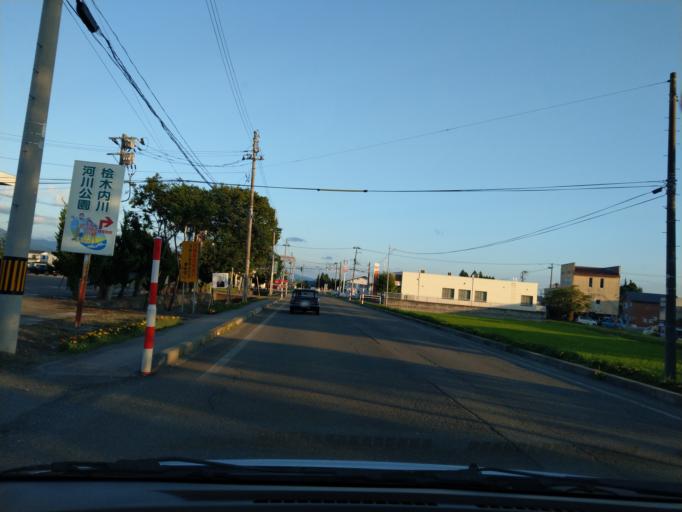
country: JP
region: Akita
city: Kakunodatemachi
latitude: 39.6565
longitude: 140.5706
